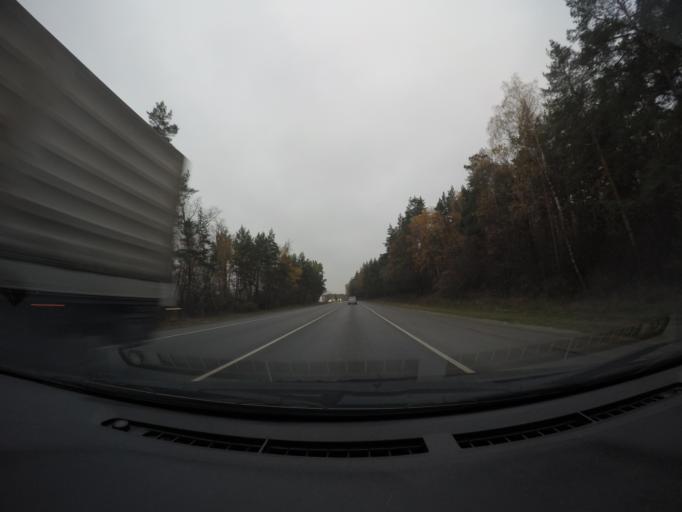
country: RU
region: Moskovskaya
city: Bronnitsy
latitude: 55.4418
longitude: 38.3190
